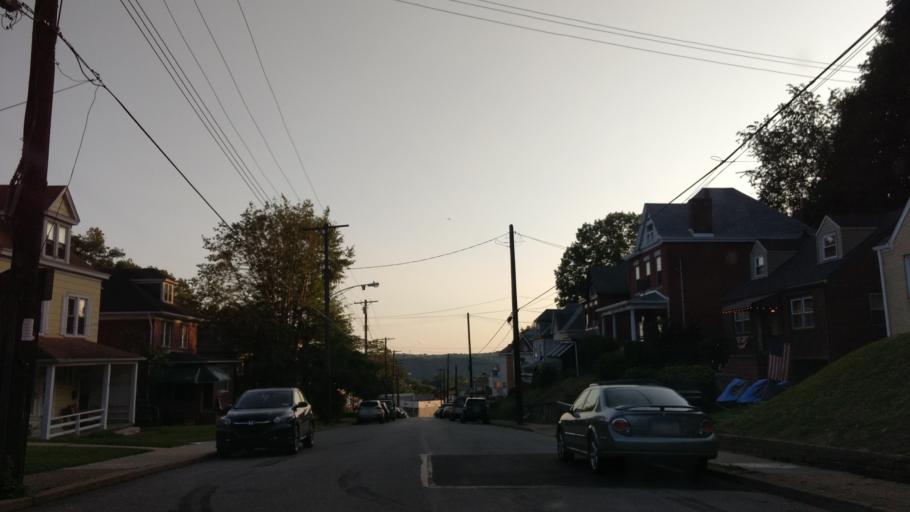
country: US
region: Pennsylvania
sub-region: Allegheny County
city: Bellevue
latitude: 40.5039
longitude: -80.0529
